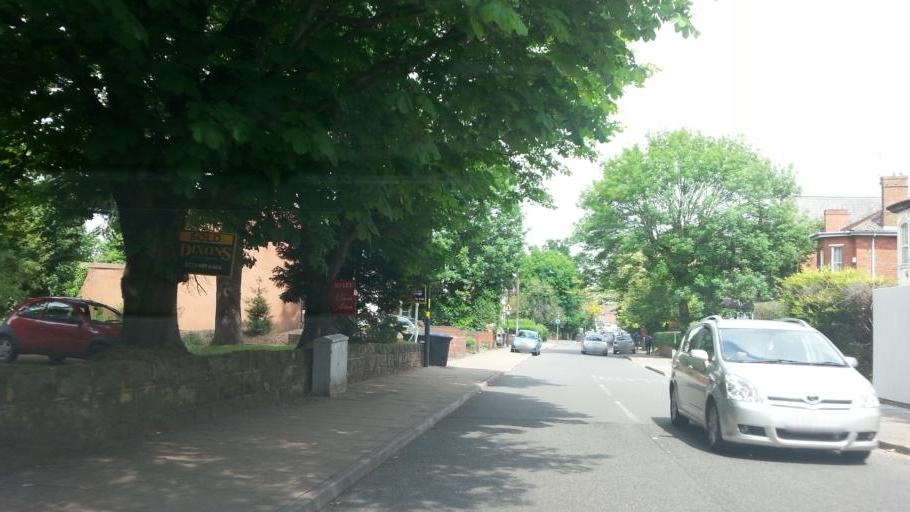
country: GB
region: England
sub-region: City and Borough of Birmingham
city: Birmingham
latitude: 52.4491
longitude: -1.8819
